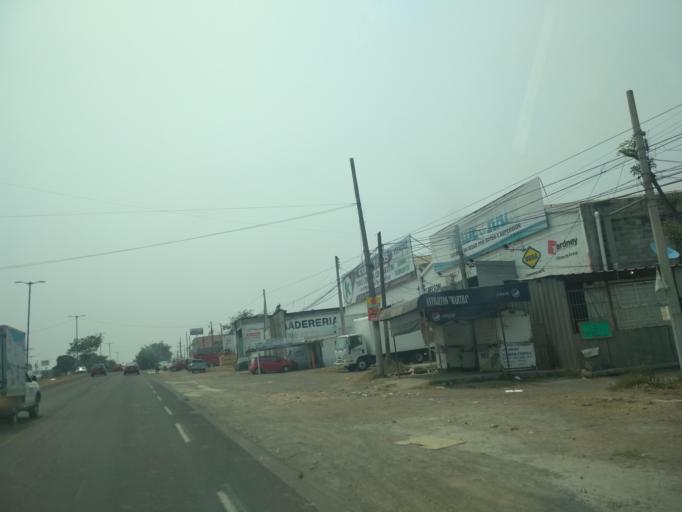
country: MX
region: Veracruz
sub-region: Veracruz
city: Lomas de Rio Medio Cuatro
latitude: 19.1681
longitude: -96.2211
